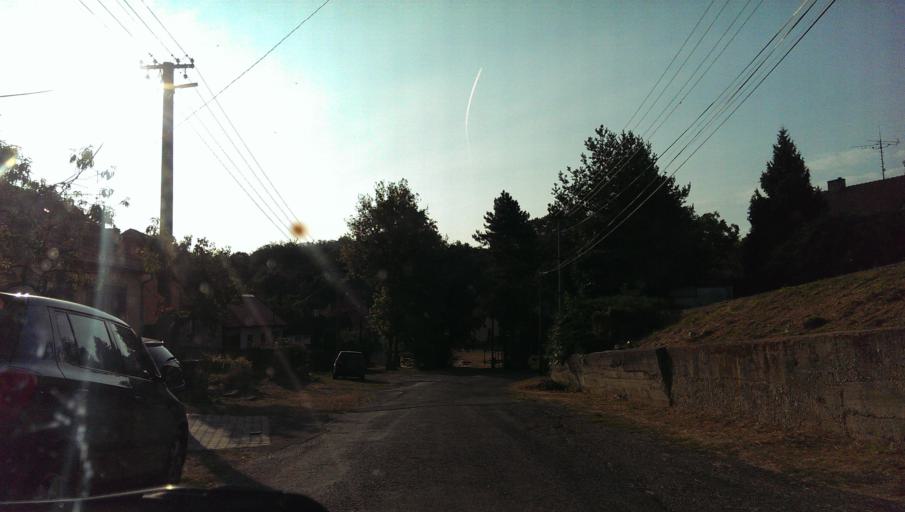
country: CZ
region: South Moravian
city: Zeravice
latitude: 49.0489
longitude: 17.2720
